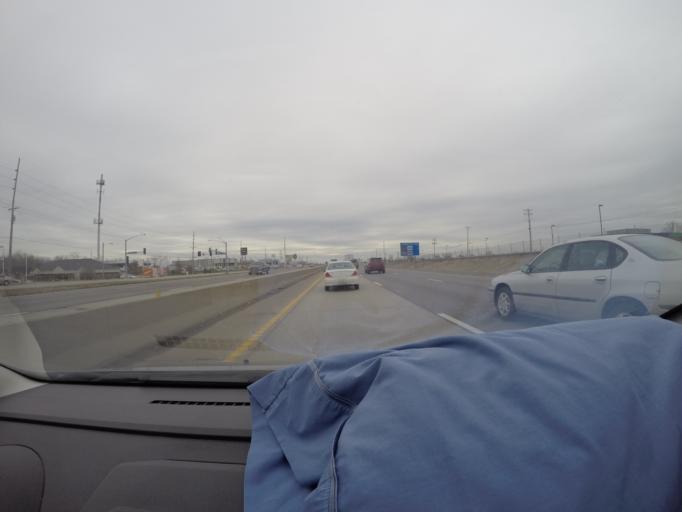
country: US
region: Missouri
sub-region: Saint Charles County
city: Saint Peters
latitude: 38.7973
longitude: -90.5801
